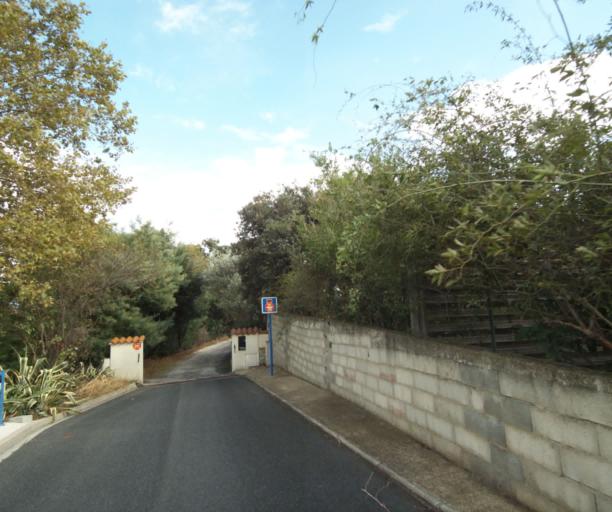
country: FR
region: Languedoc-Roussillon
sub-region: Departement des Pyrenees-Orientales
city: Argelers
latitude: 42.5473
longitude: 3.0154
